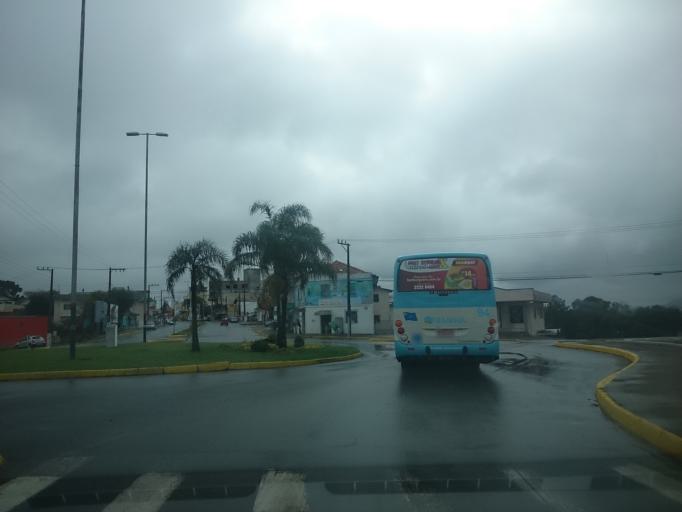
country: BR
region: Santa Catarina
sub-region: Lages
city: Lages
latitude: -27.8269
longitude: -50.3360
